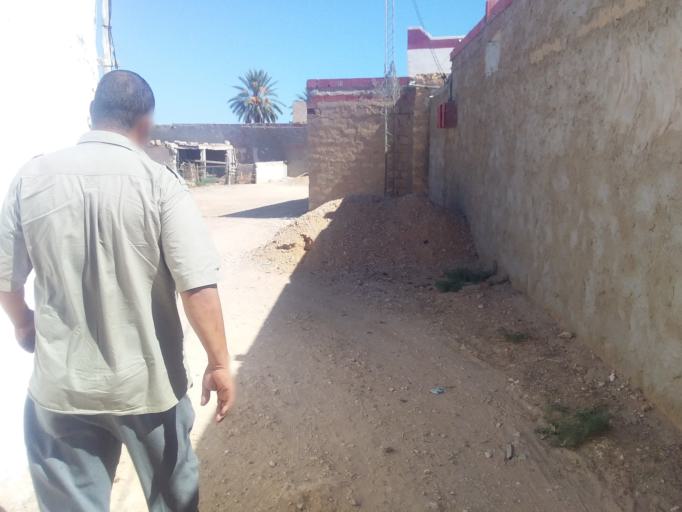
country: TN
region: Qabis
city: Matmata
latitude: 33.5836
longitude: 10.2802
